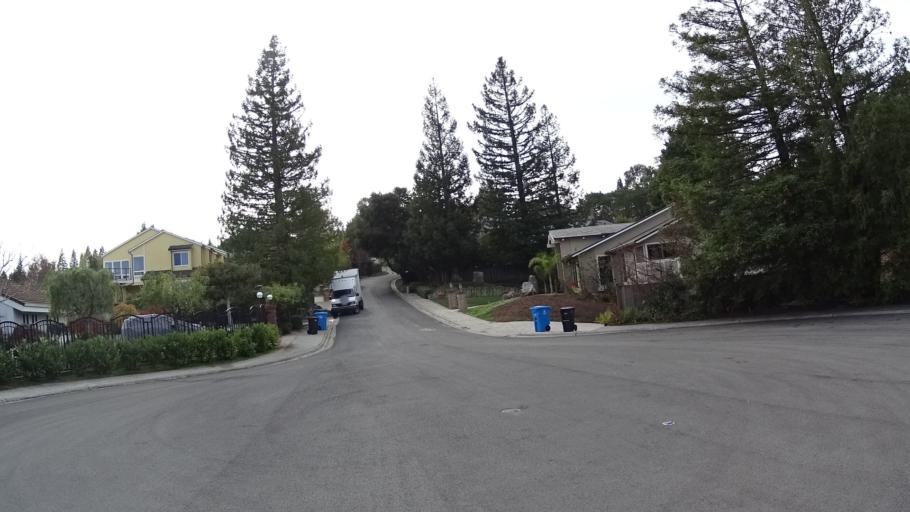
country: US
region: California
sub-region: San Mateo County
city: Hillsborough
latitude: 37.5663
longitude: -122.3844
